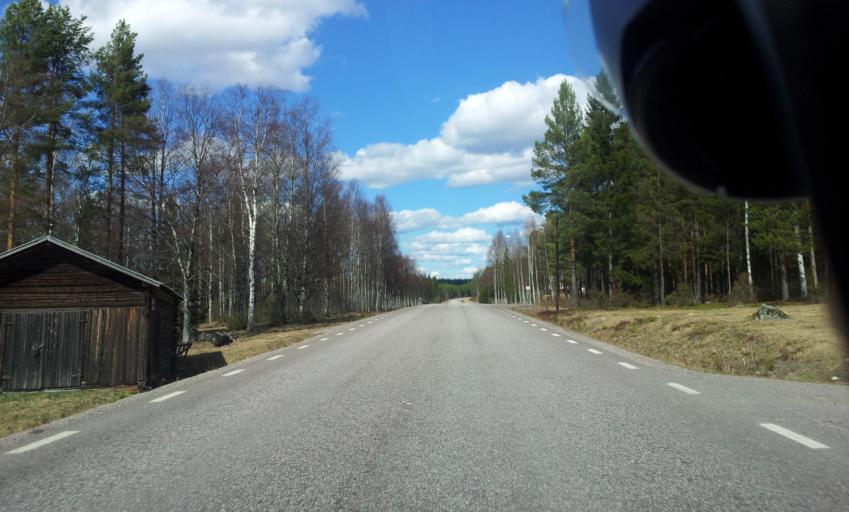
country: SE
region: Gaevleborg
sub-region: Ovanakers Kommun
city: Edsbyn
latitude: 61.2694
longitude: 15.8926
